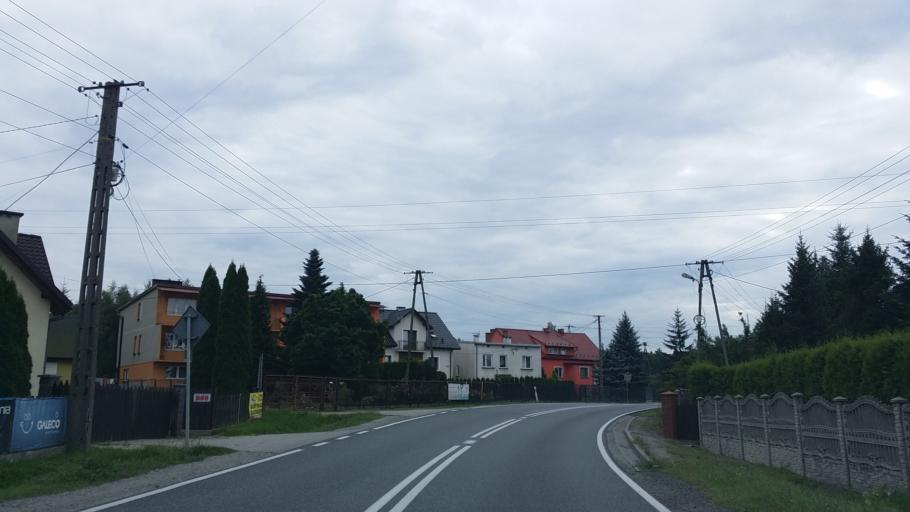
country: PL
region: Lesser Poland Voivodeship
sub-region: Powiat krakowski
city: Krzecin
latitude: 49.9617
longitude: 19.7566
